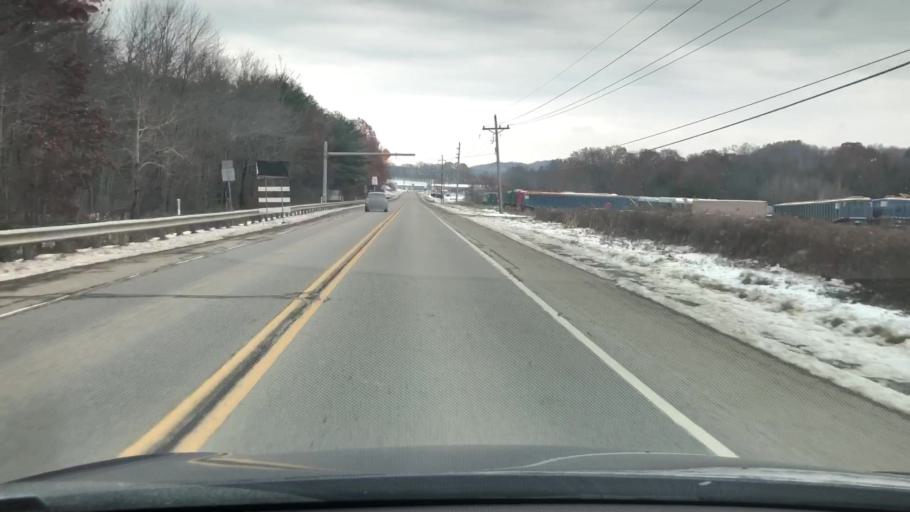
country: US
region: Pennsylvania
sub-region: Jefferson County
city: Brookville
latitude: 41.1616
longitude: -79.0982
